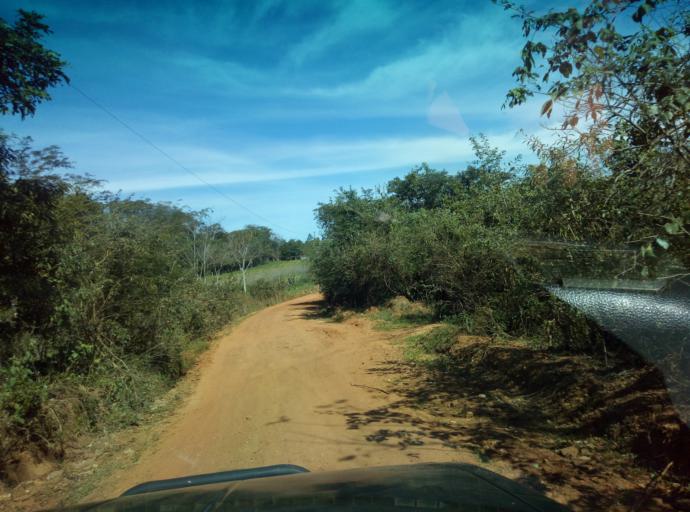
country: PY
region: Caaguazu
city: Carayao
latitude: -25.1876
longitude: -56.2549
